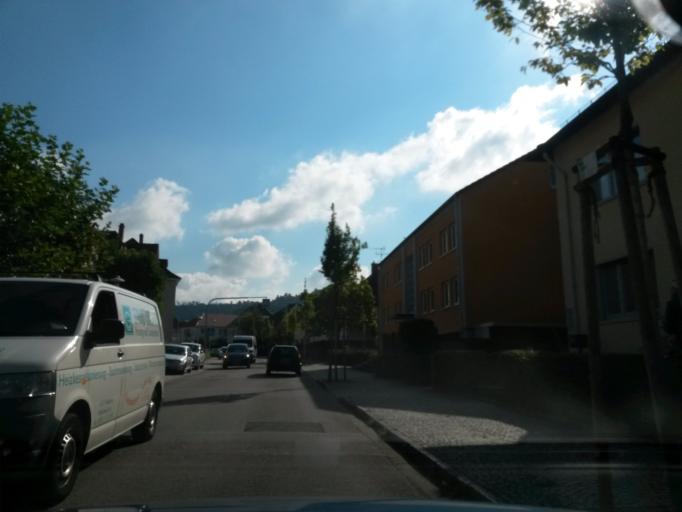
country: DE
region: Baden-Wuerttemberg
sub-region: Karlsruhe Region
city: Ettlingen
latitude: 48.9389
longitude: 8.4046
